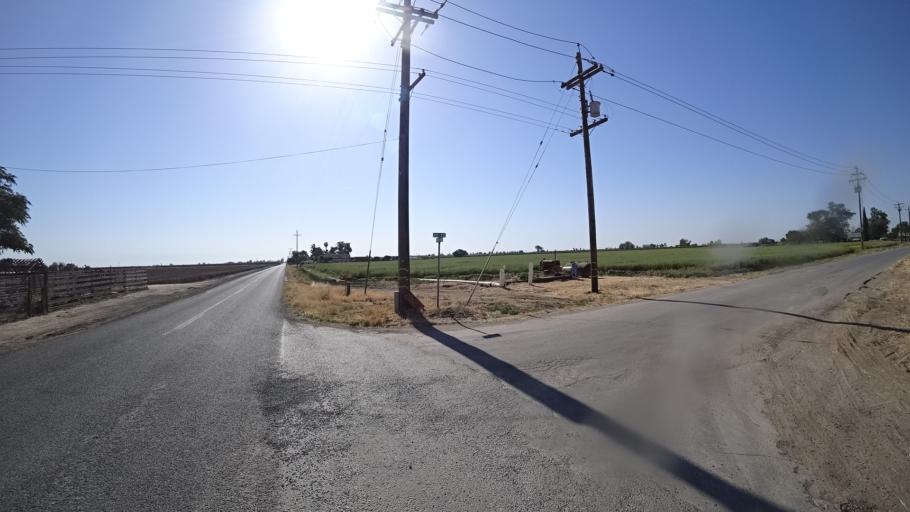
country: US
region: California
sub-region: Kings County
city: Corcoran
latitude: 36.1379
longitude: -119.5275
